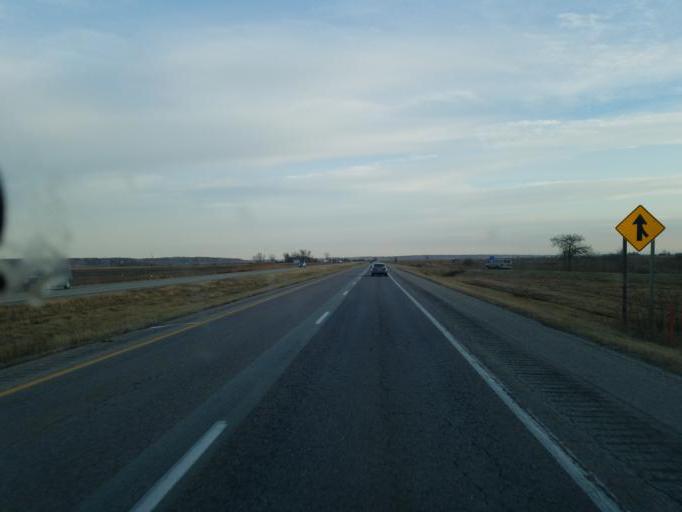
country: US
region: Iowa
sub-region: Harrison County
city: Missouri Valley
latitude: 41.5915
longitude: -95.9524
